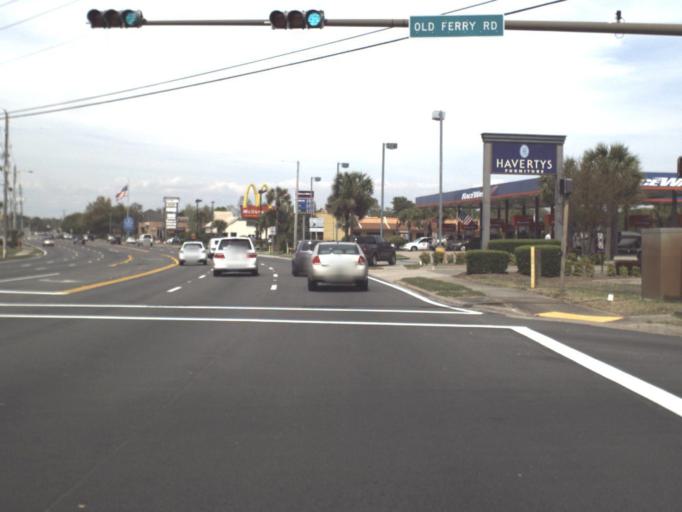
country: US
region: Florida
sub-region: Okaloosa County
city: Lake Lorraine
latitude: 30.4408
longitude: -86.5816
